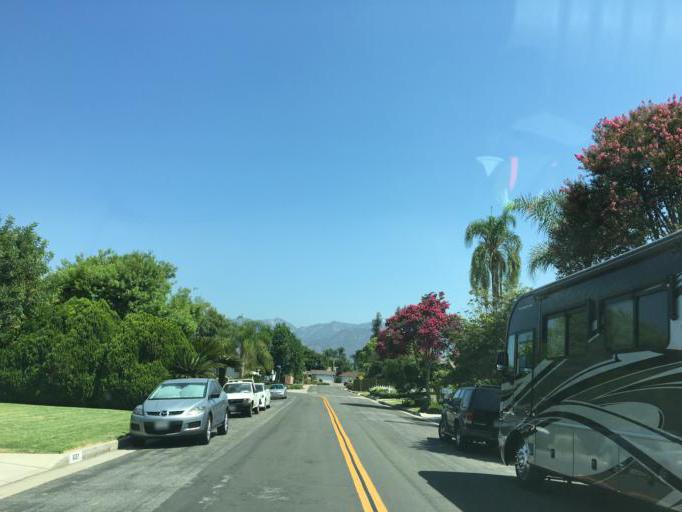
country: US
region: California
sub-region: Los Angeles County
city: San Marino
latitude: 34.1147
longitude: -118.0853
